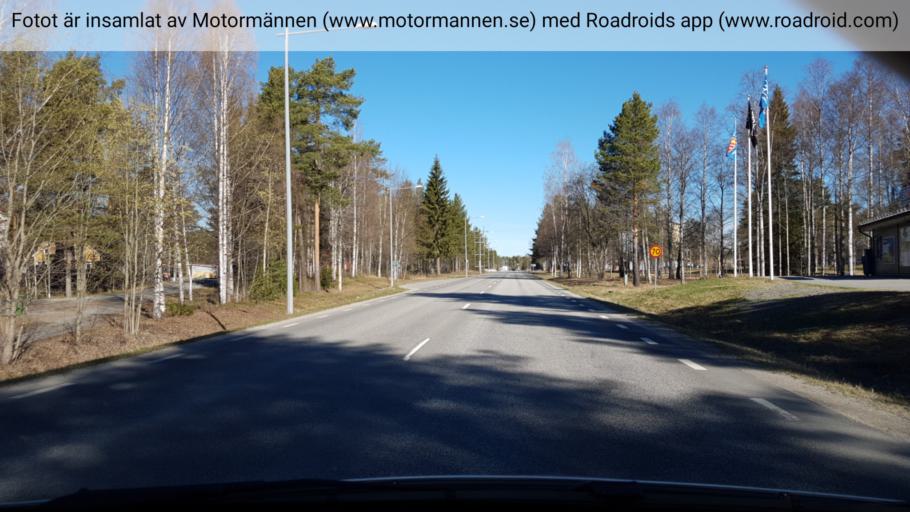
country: SE
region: Vaesterbotten
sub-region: Lycksele Kommun
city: Lycksele
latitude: 64.5797
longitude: 18.7041
